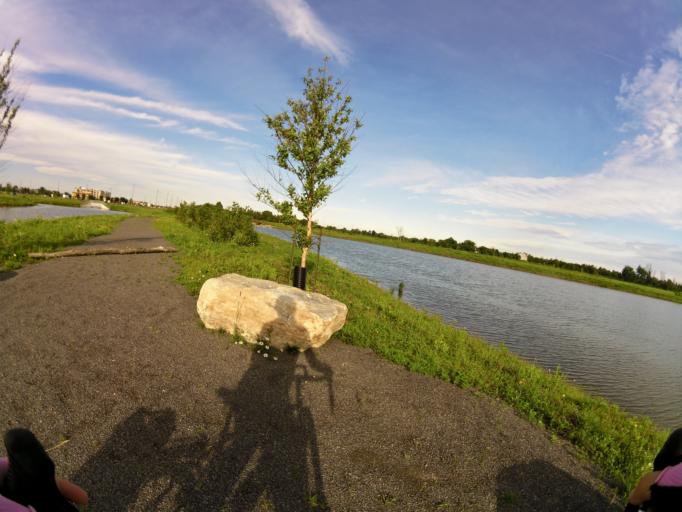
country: CA
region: Ontario
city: Bells Corners
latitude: 45.2584
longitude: -75.7733
